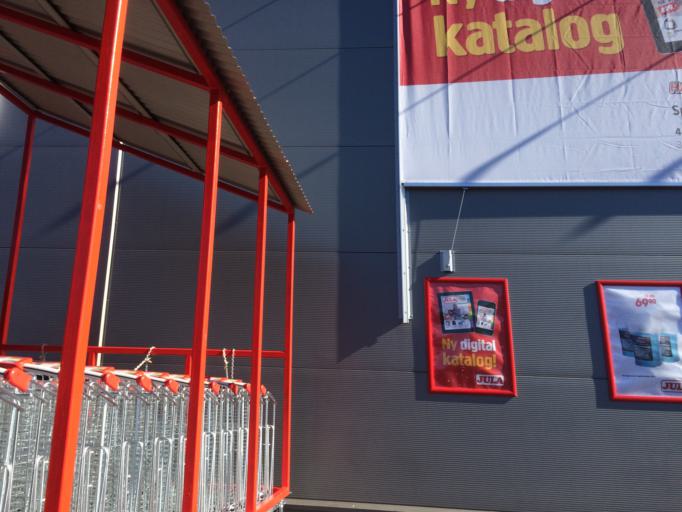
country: NO
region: Akershus
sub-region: Ski
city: Ski
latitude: 59.7258
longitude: 10.7810
